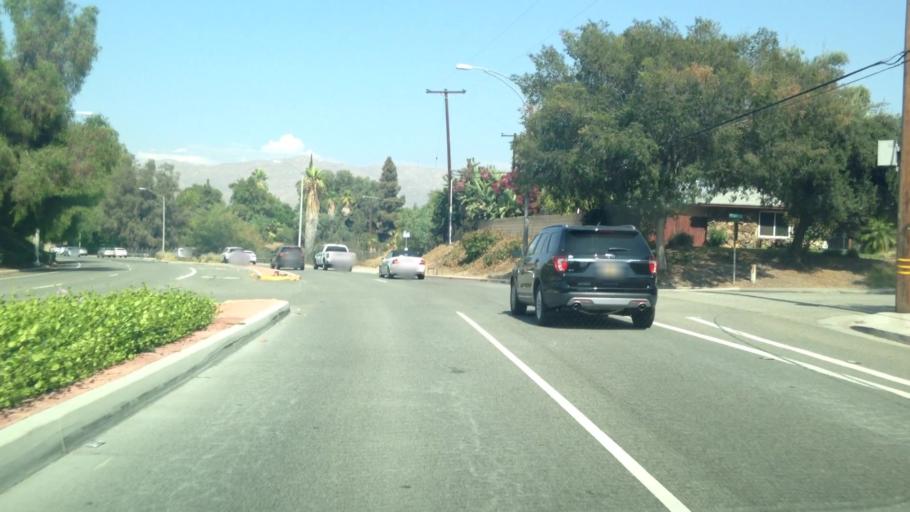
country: US
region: California
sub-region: Riverside County
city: Riverside
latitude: 33.9453
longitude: -117.3515
